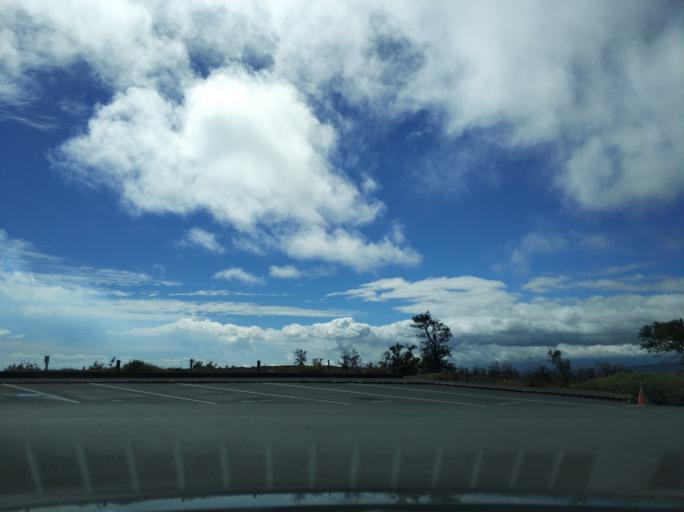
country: US
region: Hawaii
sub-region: Hawaii County
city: Volcano
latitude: 19.4200
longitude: -155.2891
